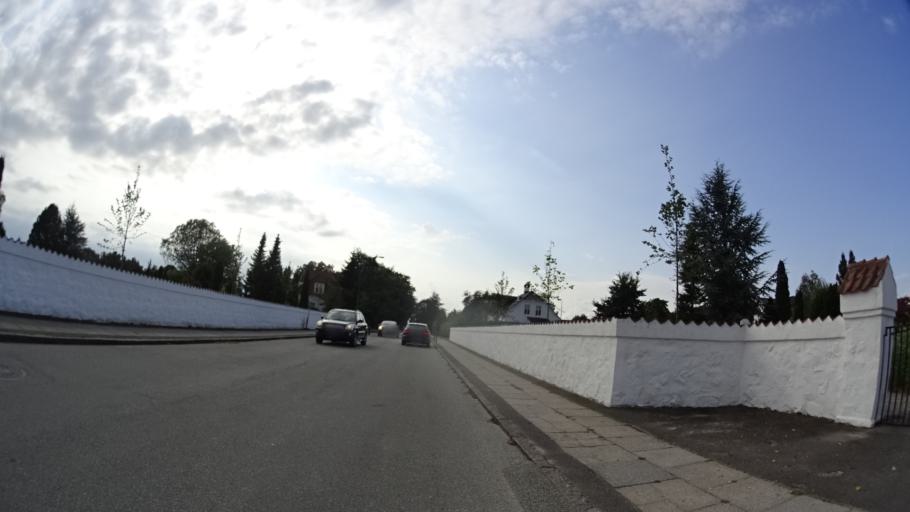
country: DK
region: Central Jutland
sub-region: Arhus Kommune
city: Stavtrup
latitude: 56.1521
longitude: 10.1011
